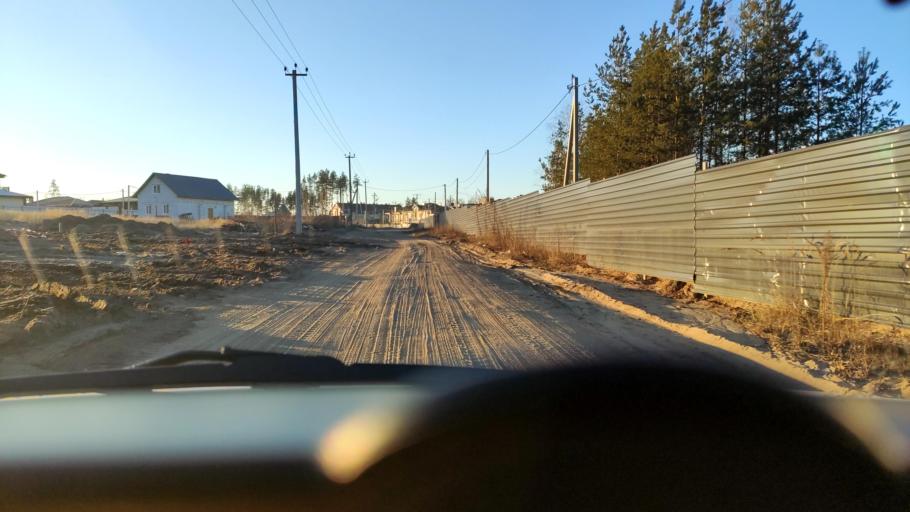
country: RU
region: Voronezj
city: Podgornoye
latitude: 51.7490
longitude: 39.1420
